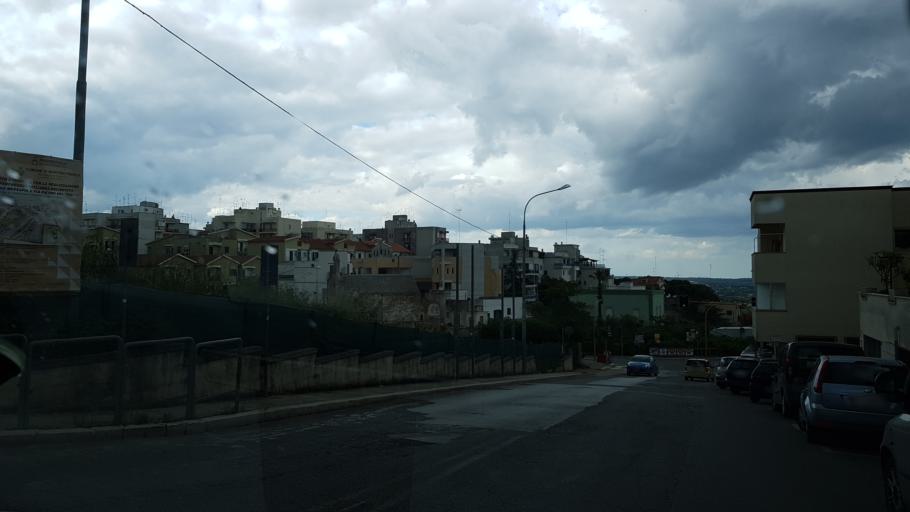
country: IT
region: Apulia
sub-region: Provincia di Taranto
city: Martina Franca
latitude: 40.7000
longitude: 17.3466
